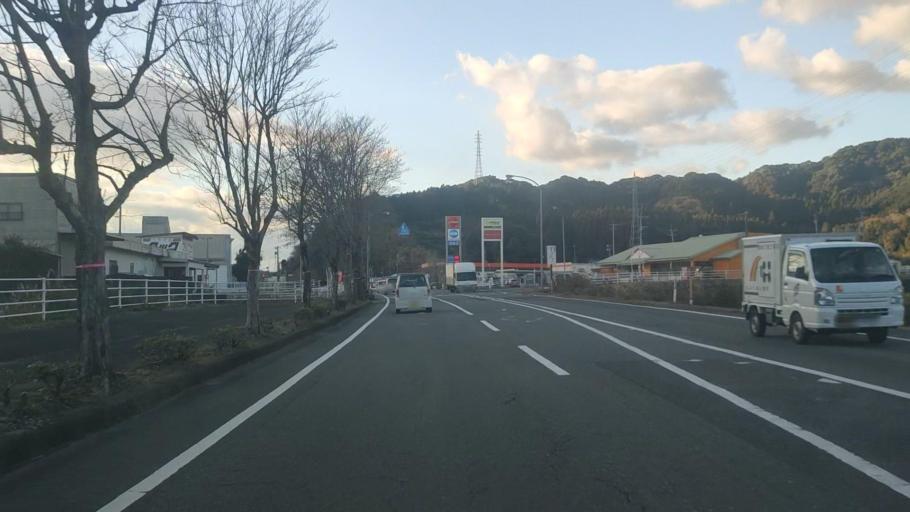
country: JP
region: Saga Prefecture
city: Takeocho-takeo
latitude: 33.2885
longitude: 130.1328
